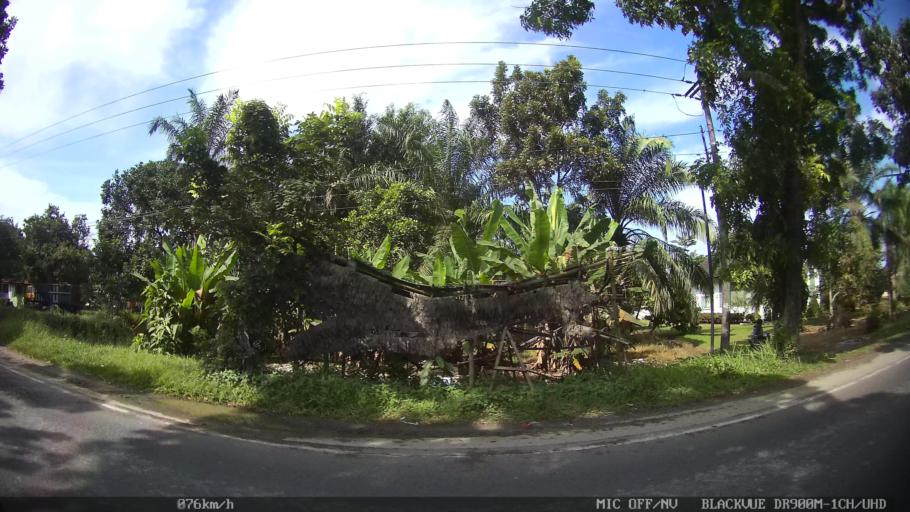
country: ID
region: North Sumatra
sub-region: Kabupaten Langkat
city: Stabat
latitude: 3.7323
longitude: 98.4923
